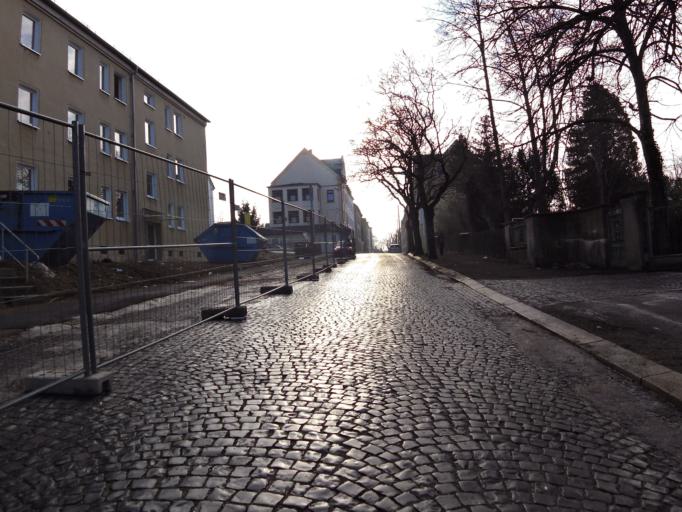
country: DE
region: Saxony
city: Glauchau
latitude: 50.8219
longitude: 12.5488
